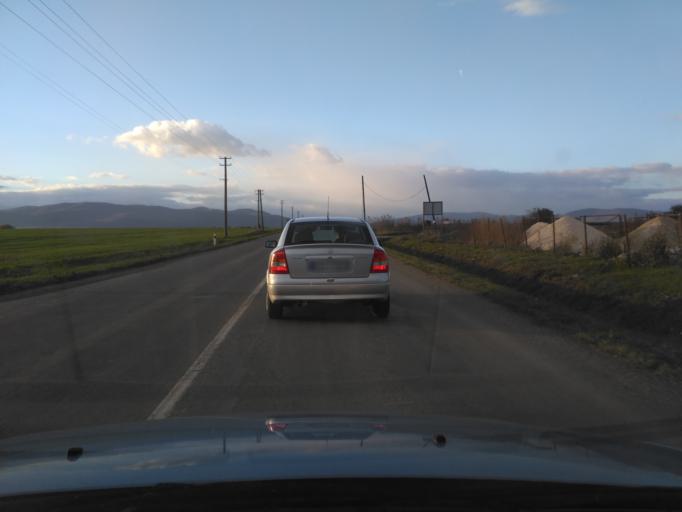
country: SK
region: Kosicky
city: Secovce
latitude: 48.6568
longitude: 21.6696
